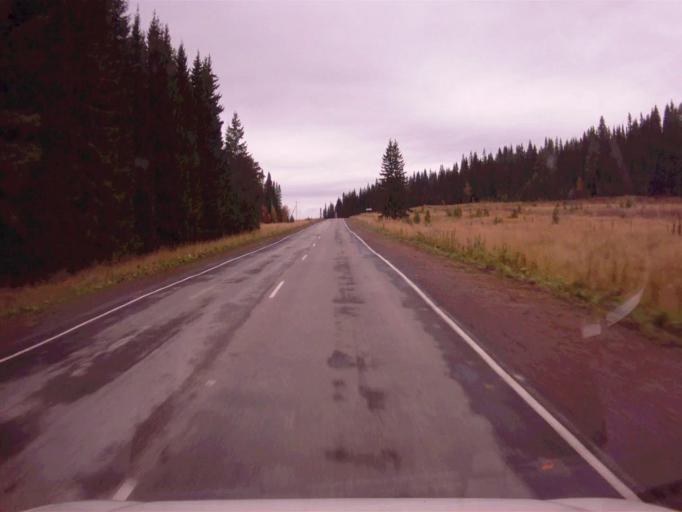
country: RU
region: Chelyabinsk
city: Nyazepetrovsk
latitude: 56.0663
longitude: 59.6407
